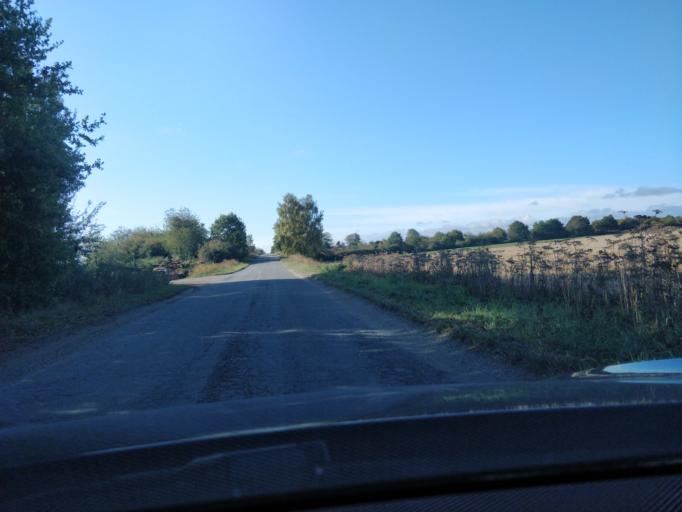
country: FR
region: Ile-de-France
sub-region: Departement de l'Essonne
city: Forges-les-Bains
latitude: 48.6130
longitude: 2.1053
